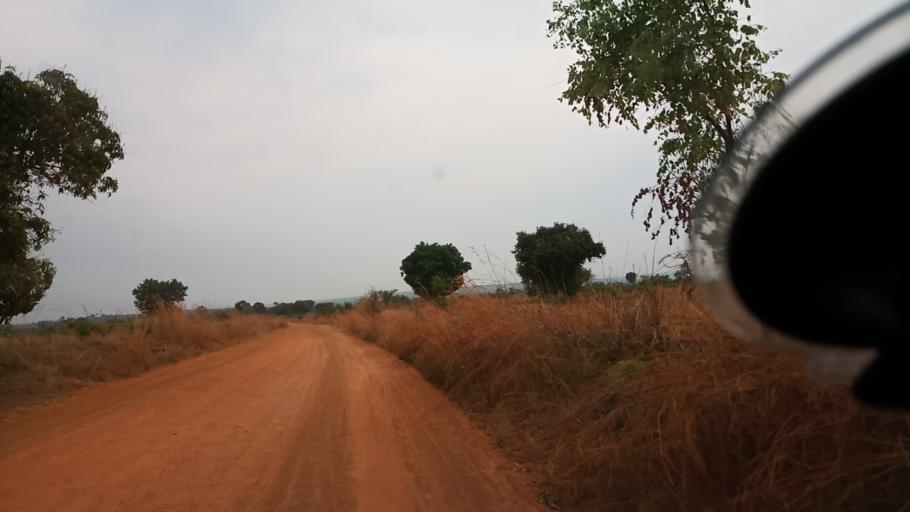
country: ZM
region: Luapula
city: Nchelenge
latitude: -9.1252
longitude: 28.3032
